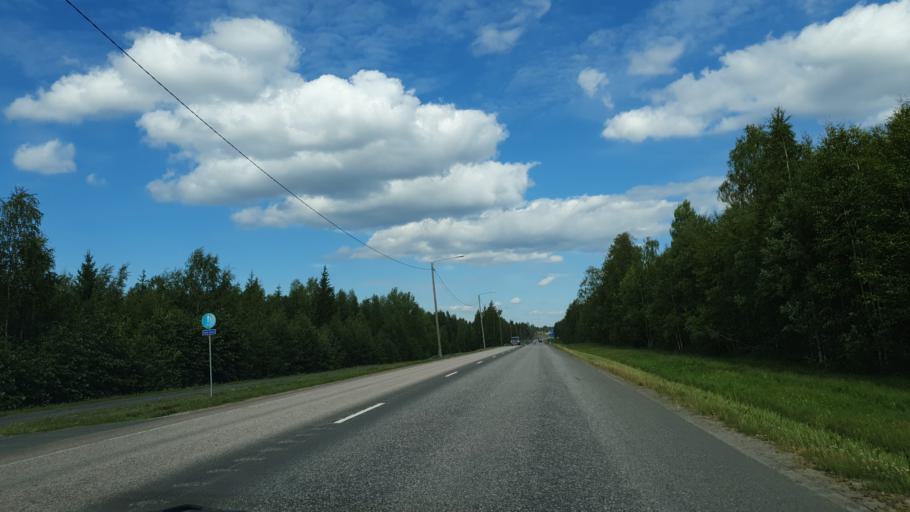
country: FI
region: Kainuu
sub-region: Kajaani
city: Kajaani
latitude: 64.2637
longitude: 27.8412
